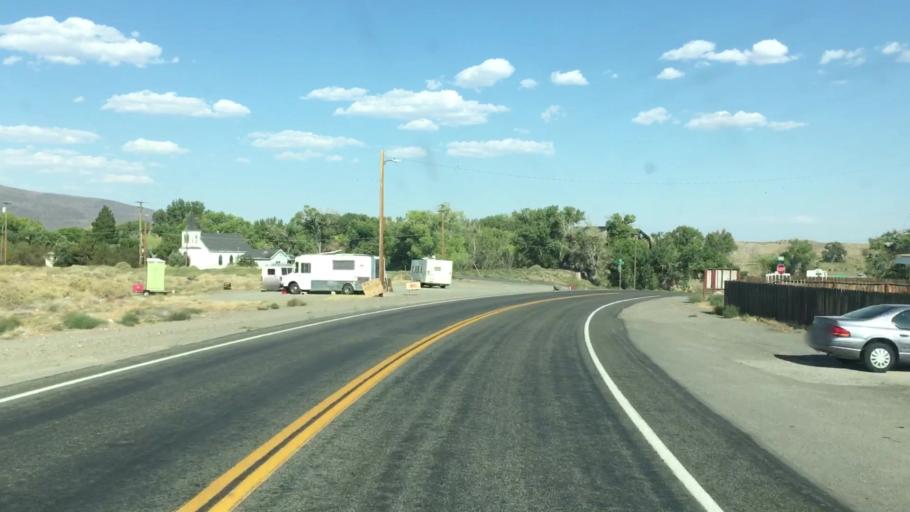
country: US
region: Nevada
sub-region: Lyon County
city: Fernley
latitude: 39.6326
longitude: -119.2856
